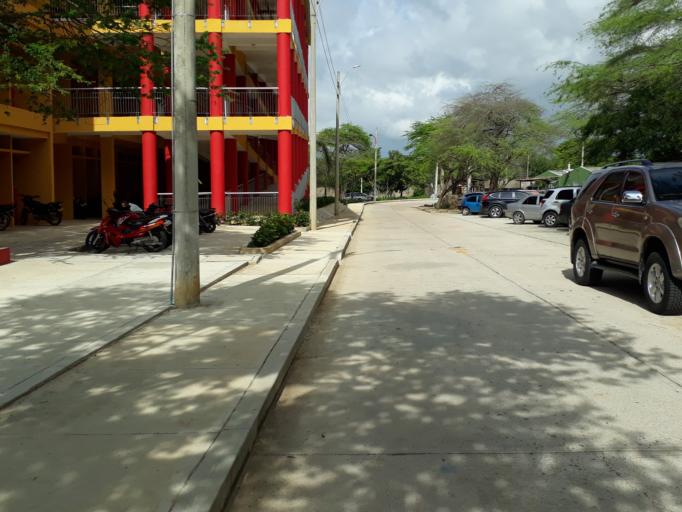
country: CO
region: La Guajira
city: Riohacha
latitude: 11.5117
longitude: -72.8706
